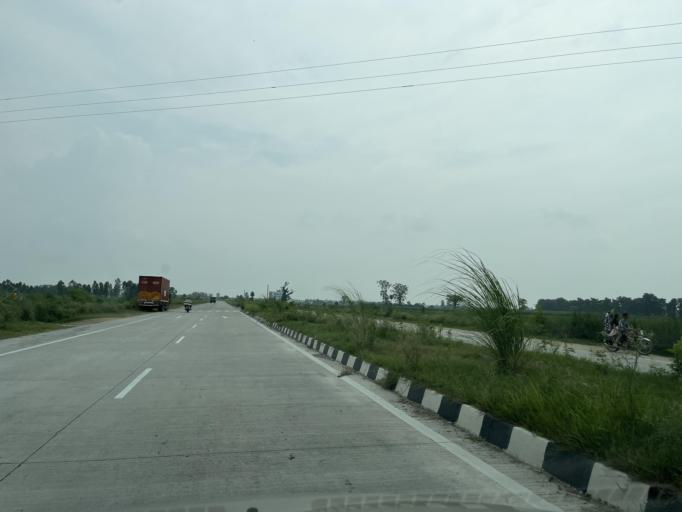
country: IN
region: Uttarakhand
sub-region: Udham Singh Nagar
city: Kashipur
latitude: 29.1843
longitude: 78.9397
